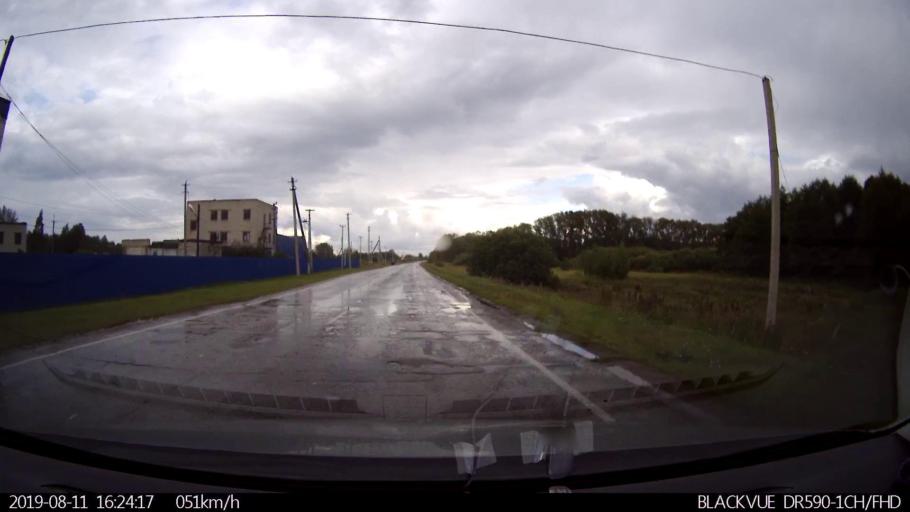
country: RU
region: Ulyanovsk
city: Mayna
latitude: 54.0996
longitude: 47.5931
